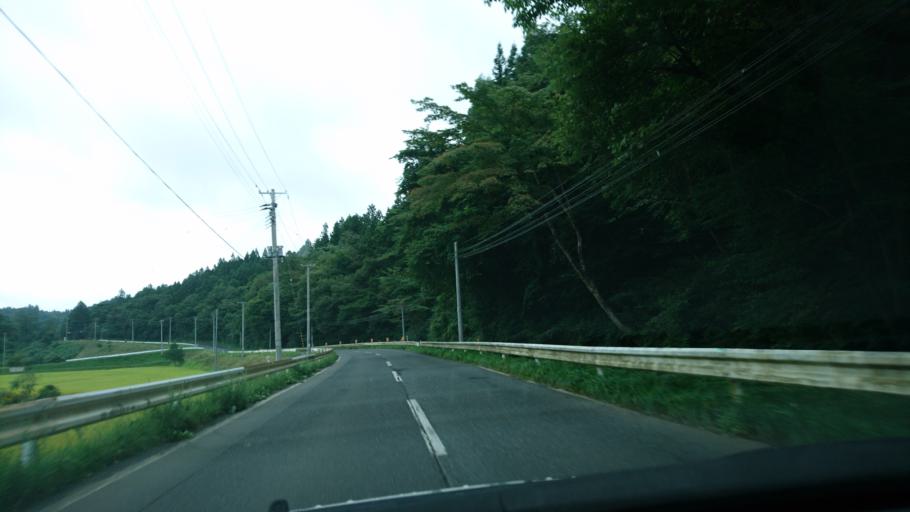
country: JP
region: Iwate
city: Ichinoseki
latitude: 38.9122
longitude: 141.0736
